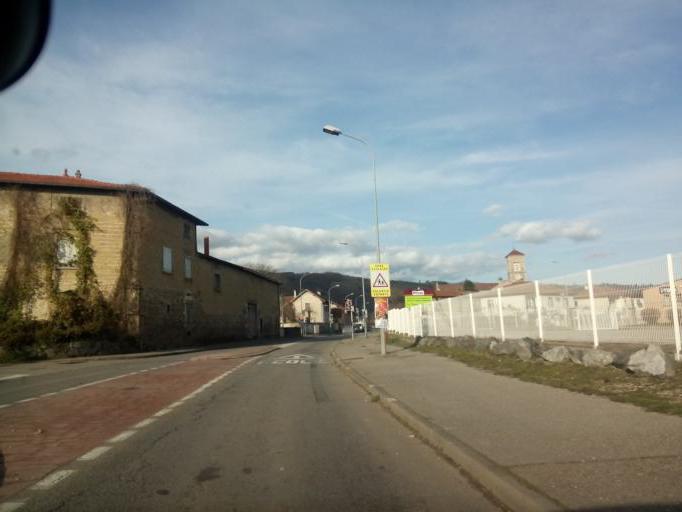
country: FR
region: Rhone-Alpes
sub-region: Departement de l'Isere
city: Sablons
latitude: 45.3176
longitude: 4.7755
